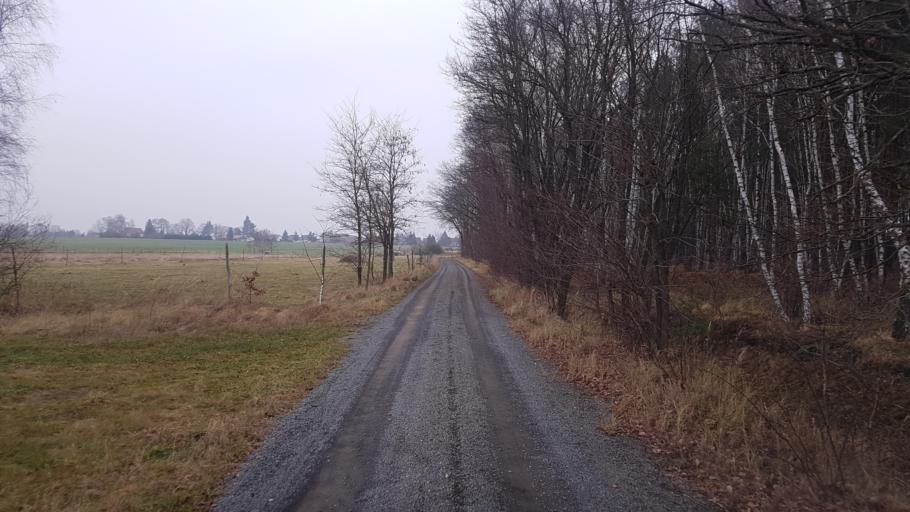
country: DE
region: Brandenburg
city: Plessa
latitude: 51.5265
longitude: 13.6274
